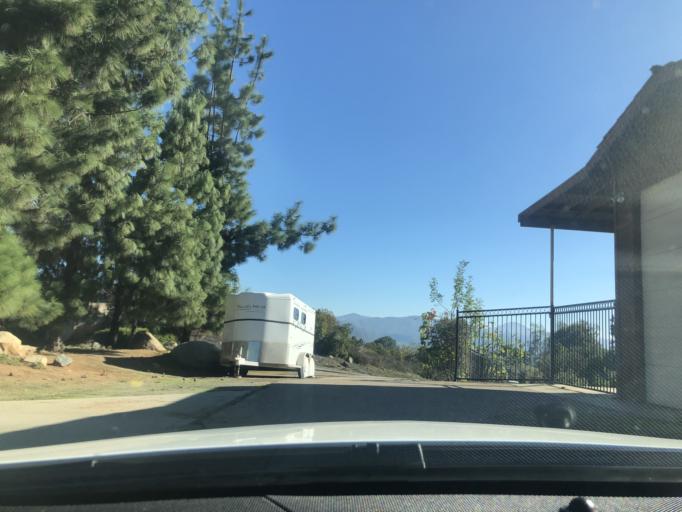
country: US
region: California
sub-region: San Diego County
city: Casa de Oro-Mount Helix
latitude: 32.7738
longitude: -116.9508
